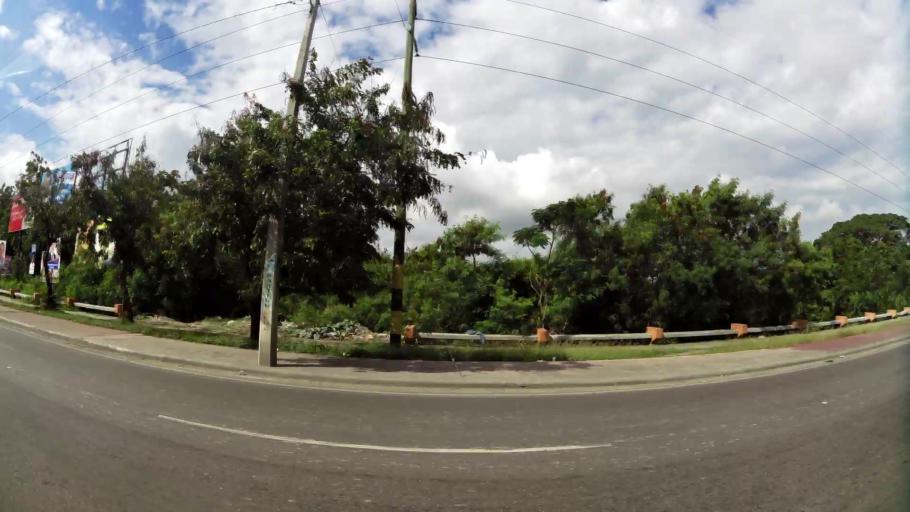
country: DO
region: Santiago
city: Santiago de los Caballeros
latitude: 19.4680
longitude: -70.7142
